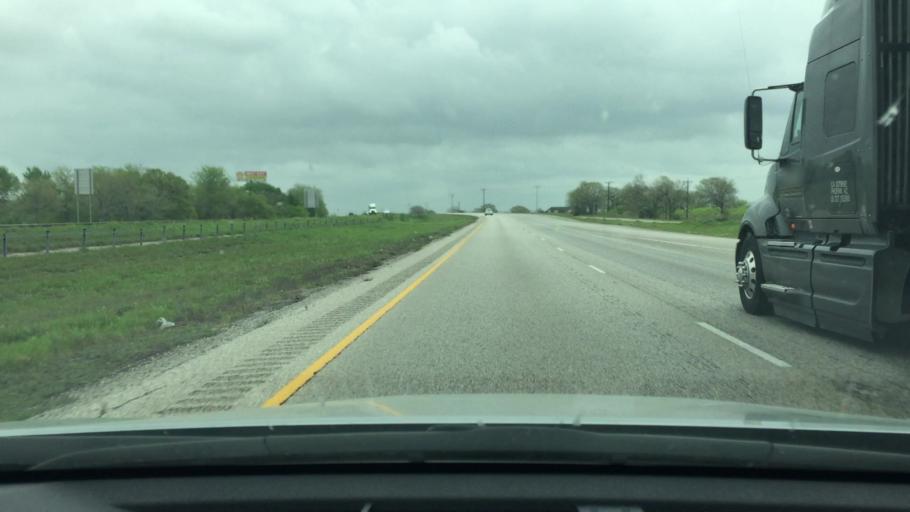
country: US
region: Texas
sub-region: Gonzales County
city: Waelder
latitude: 29.6694
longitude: -97.2993
